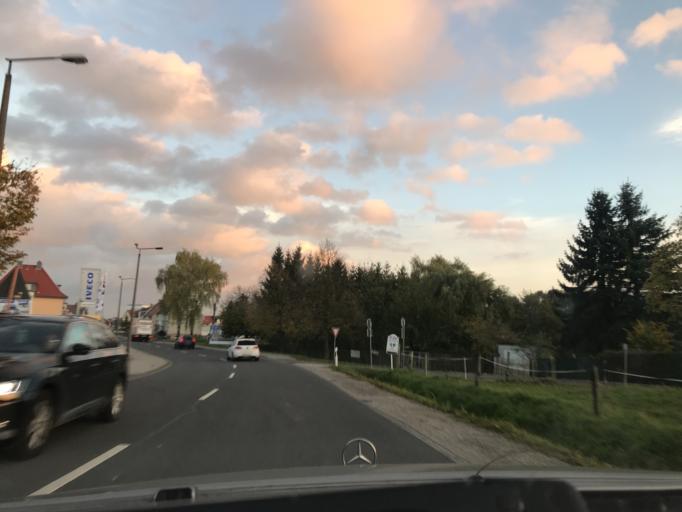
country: DE
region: Thuringia
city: Dingelstadt
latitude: 51.3187
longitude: 10.3082
